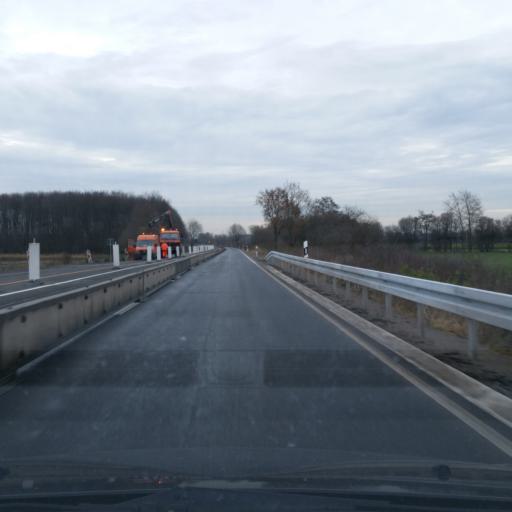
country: DE
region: North Rhine-Westphalia
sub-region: Regierungsbezirk Munster
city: Isselburg
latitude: 51.8113
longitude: 6.5315
